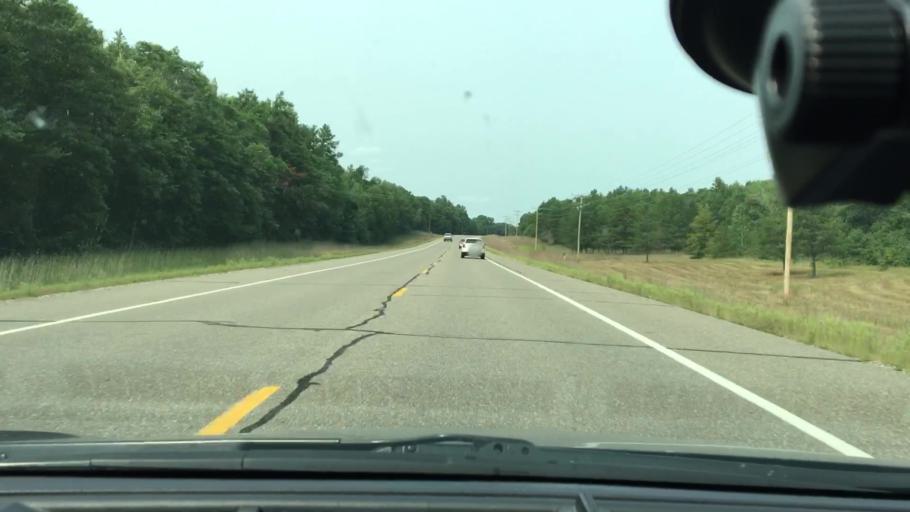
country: US
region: Minnesota
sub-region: Crow Wing County
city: Cross Lake
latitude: 46.6048
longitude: -94.1309
